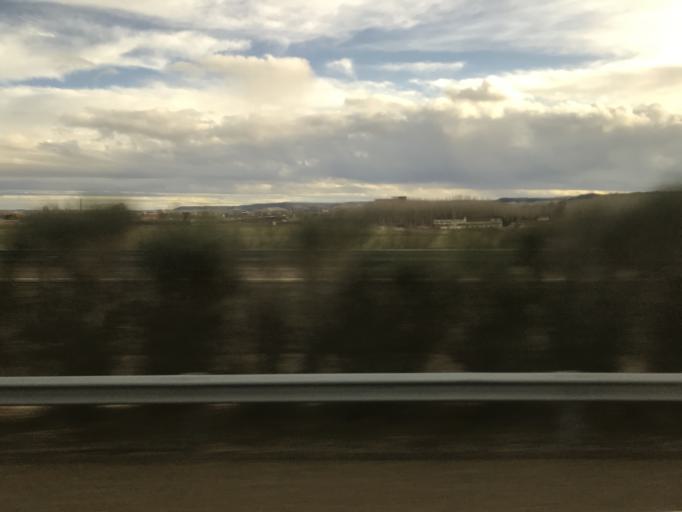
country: ES
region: Castille and Leon
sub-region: Provincia de Palencia
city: Grijota
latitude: 42.0412
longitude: -4.5529
